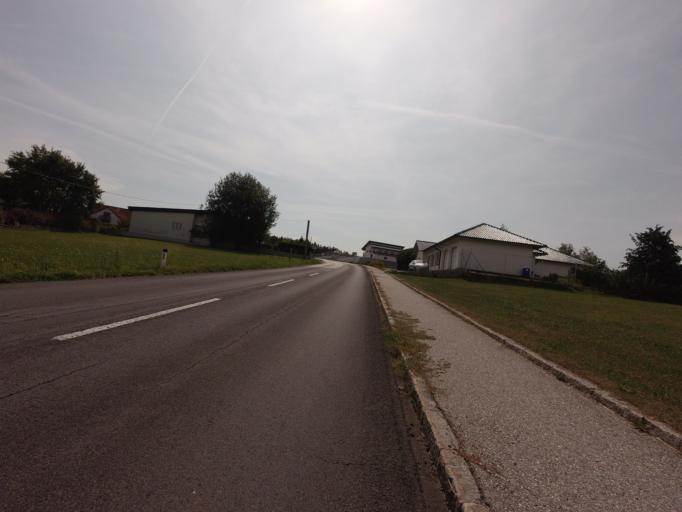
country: AT
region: Upper Austria
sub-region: Politischer Bezirk Urfahr-Umgebung
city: Reichenthal
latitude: 48.5404
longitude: 14.3727
